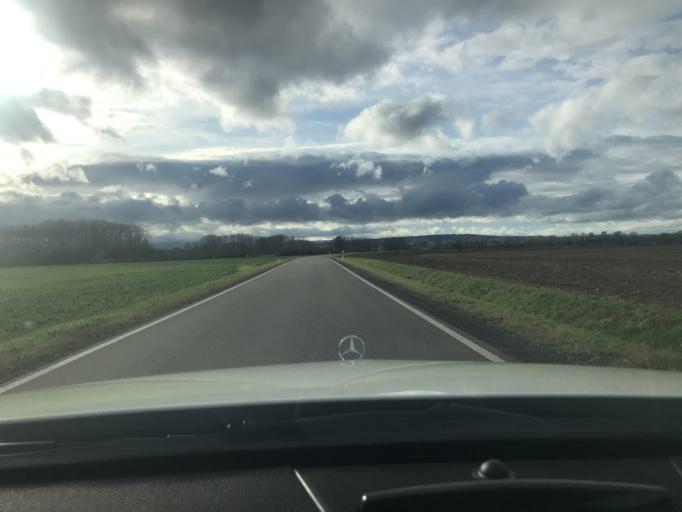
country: DE
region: Thuringia
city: Trochtelborn
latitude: 50.9875
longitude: 10.8042
